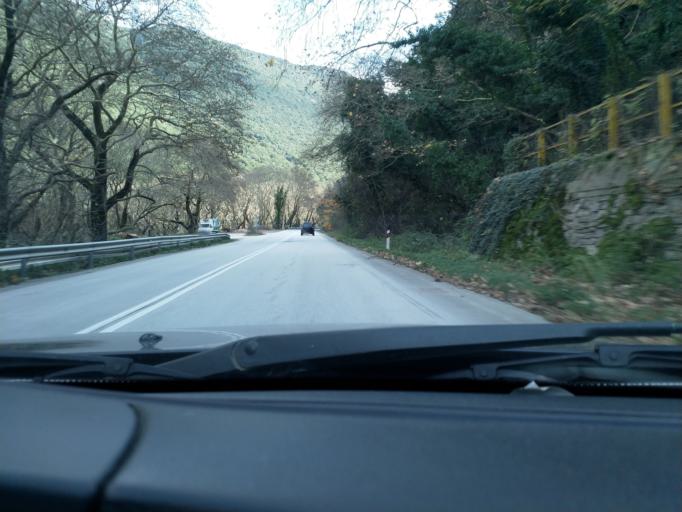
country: GR
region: Epirus
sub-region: Nomos Prevezis
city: Pappadates
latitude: 39.3964
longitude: 20.8471
